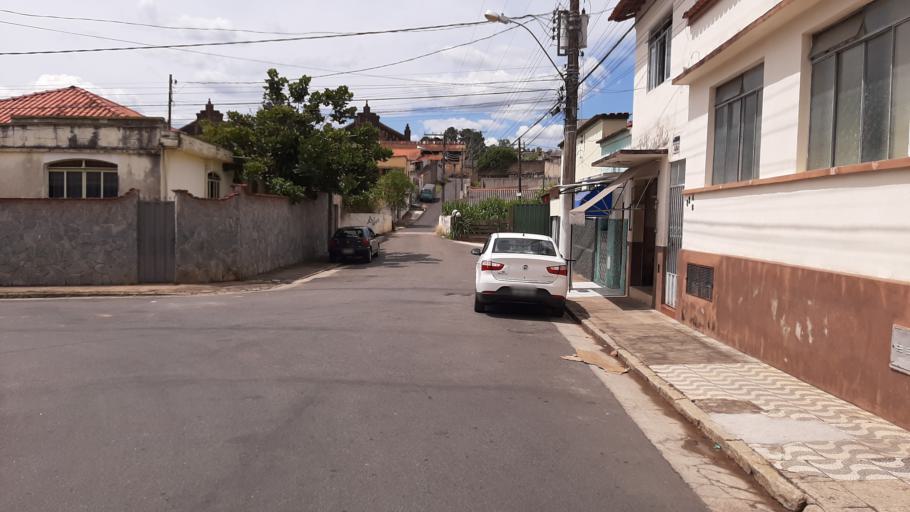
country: BR
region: Minas Gerais
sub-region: Lavras
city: Lavras
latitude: -21.2277
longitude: -44.9974
